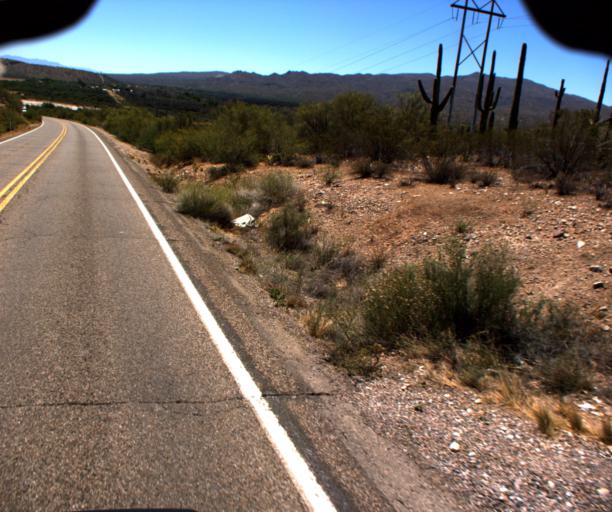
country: US
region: Arizona
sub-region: Pinal County
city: Kearny
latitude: 33.0541
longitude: -110.8988
